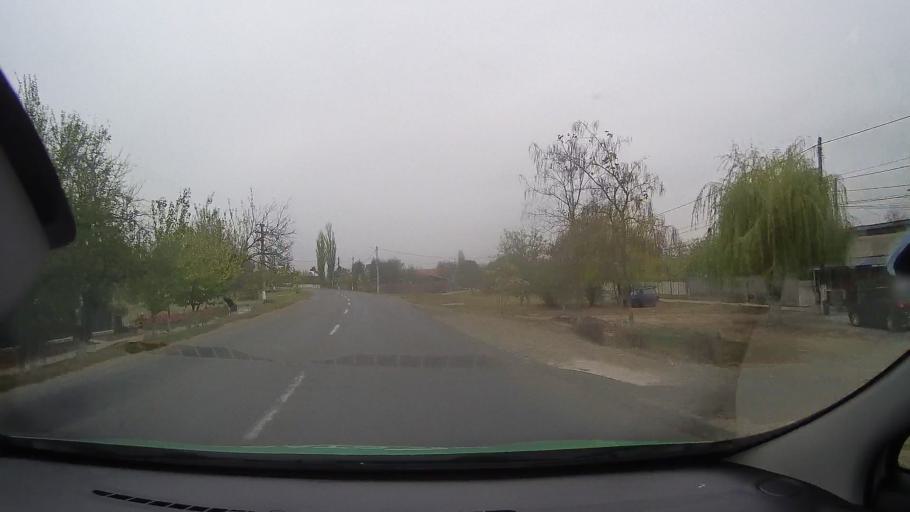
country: RO
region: Ialomita
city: Tandarei
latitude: 44.6535
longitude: 27.6546
